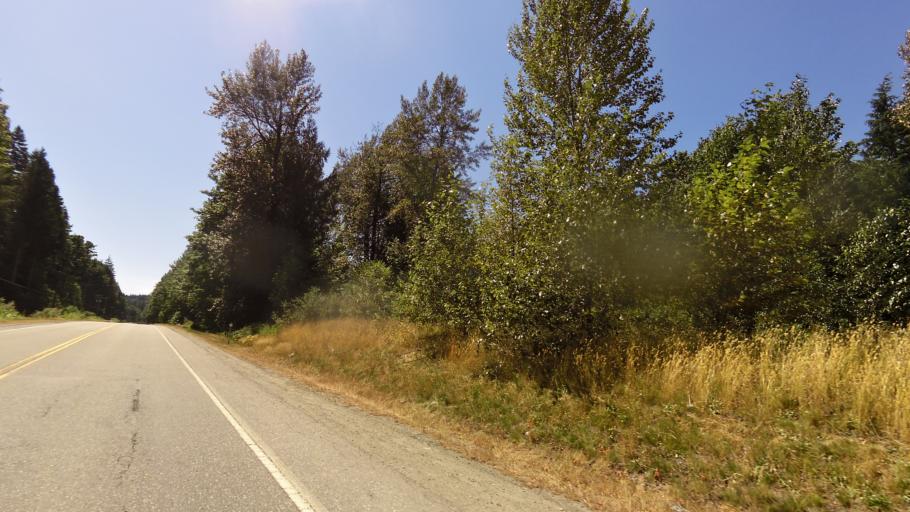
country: CA
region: British Columbia
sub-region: Fraser Valley Regional District
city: Chilliwack
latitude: 49.2387
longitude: -122.0022
